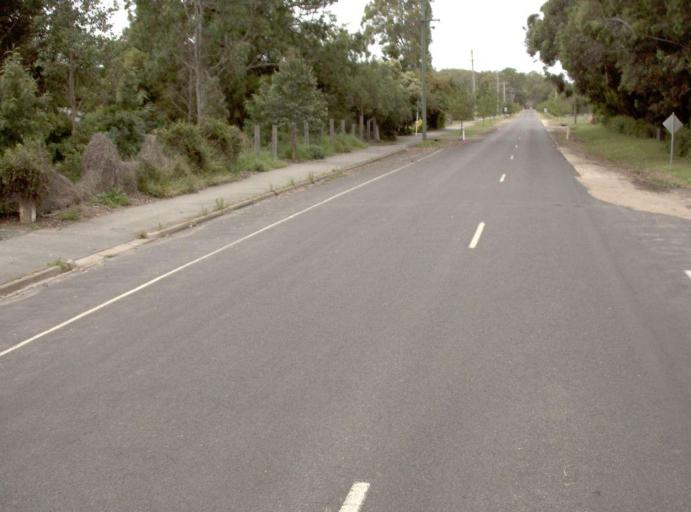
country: AU
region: Victoria
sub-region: Wellington
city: Sale
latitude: -37.8444
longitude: 147.0725
